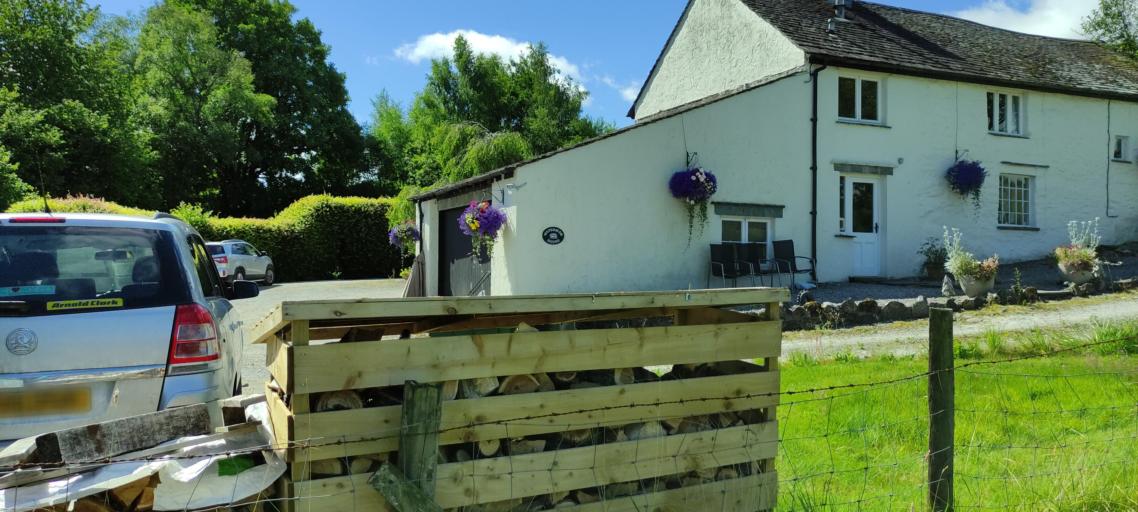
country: GB
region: England
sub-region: Cumbria
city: Ambleside
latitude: 54.3700
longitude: -2.9923
